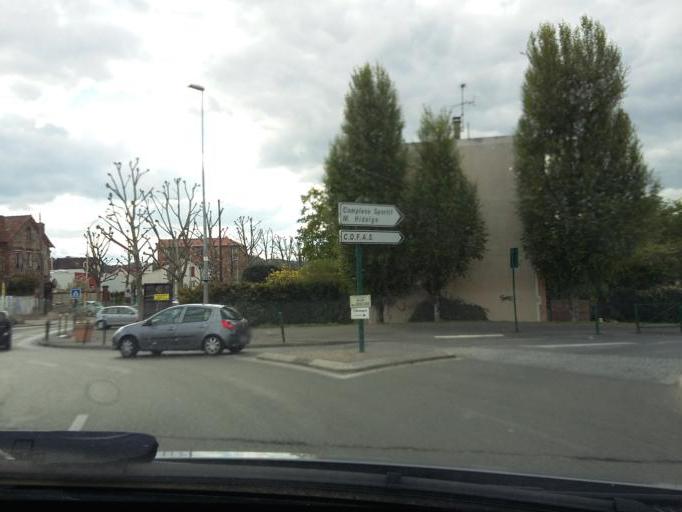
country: FR
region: Ile-de-France
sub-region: Departement du Val-d'Oise
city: Saint-Gratien
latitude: 48.9674
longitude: 2.2738
